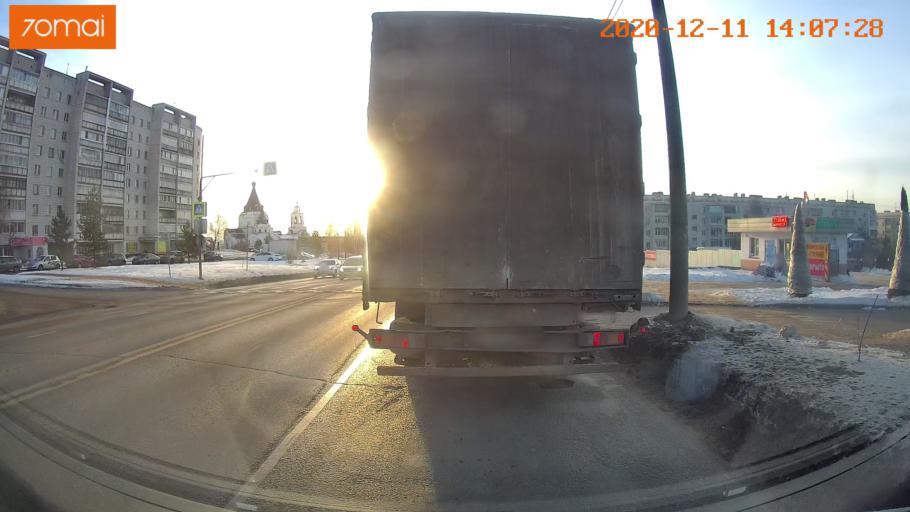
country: RU
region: Kostroma
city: Oktyabr'skiy
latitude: 57.7378
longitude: 40.9987
